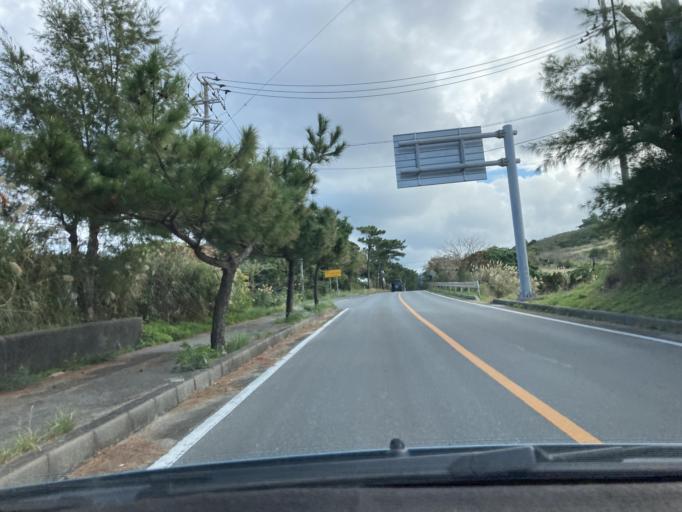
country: JP
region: Okinawa
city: Nago
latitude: 26.8646
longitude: 128.2587
